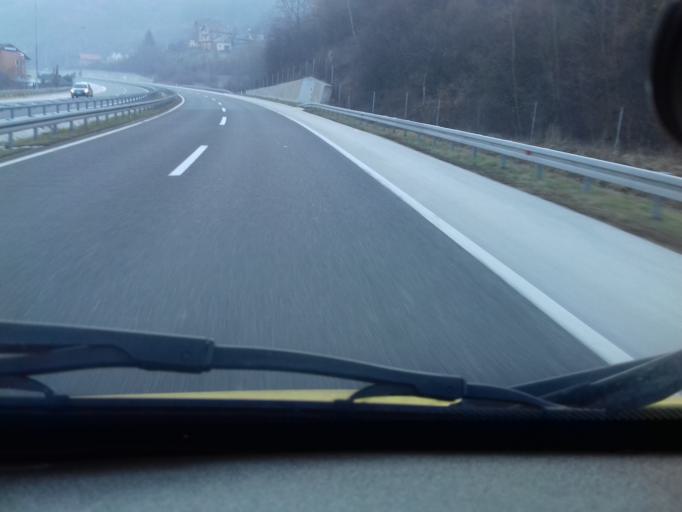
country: BA
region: Federation of Bosnia and Herzegovina
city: Kakanj
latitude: 44.1005
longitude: 18.1068
